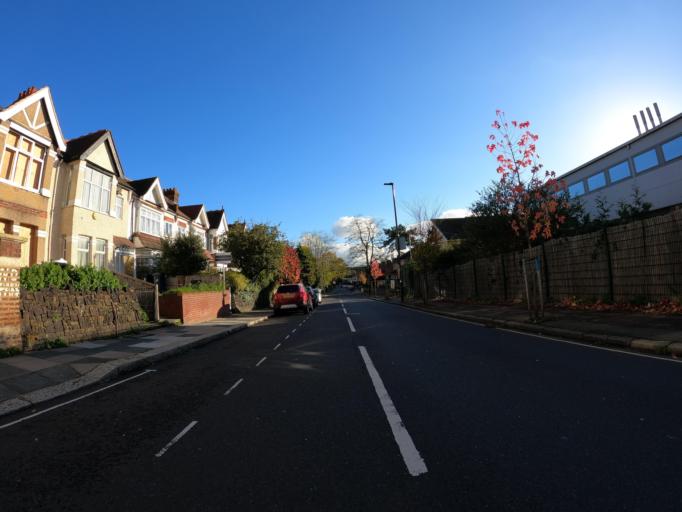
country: GB
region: England
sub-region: Greater London
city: Brentford
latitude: 51.4931
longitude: -0.3131
